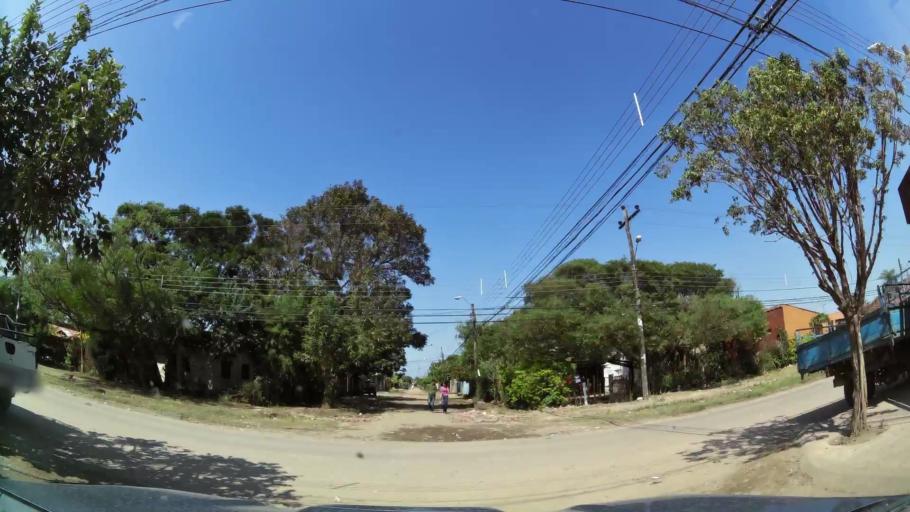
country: BO
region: Santa Cruz
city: Santa Cruz de la Sierra
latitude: -17.7384
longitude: -63.1506
